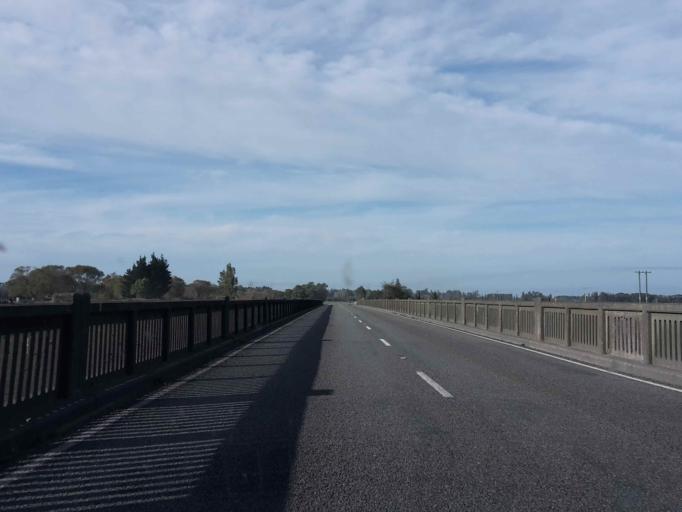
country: NZ
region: Canterbury
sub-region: Timaru District
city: Pleasant Point
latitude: -44.0615
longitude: 171.3815
